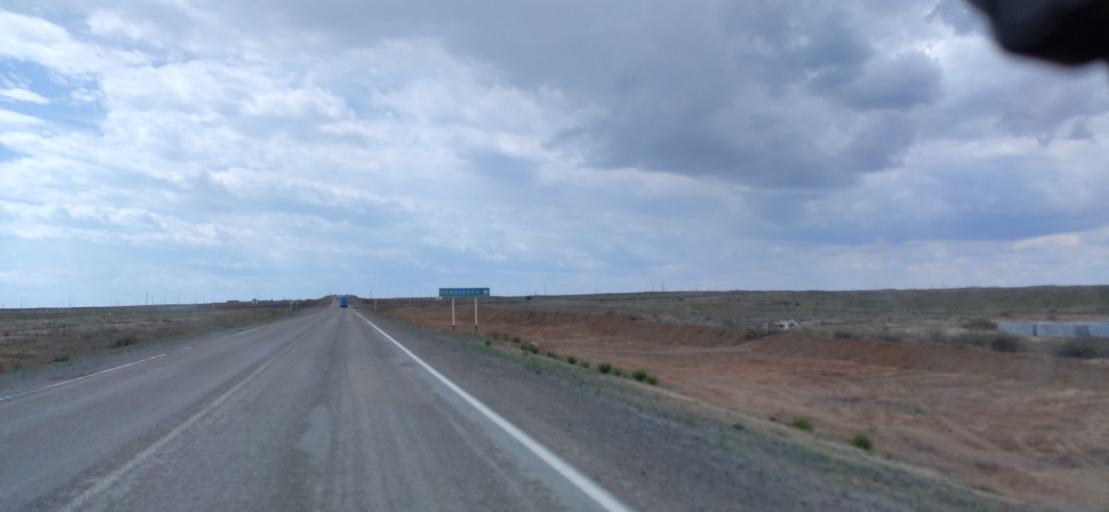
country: KZ
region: Qaraghandy
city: Saryshaghan
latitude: 46.0447
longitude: 73.5946
